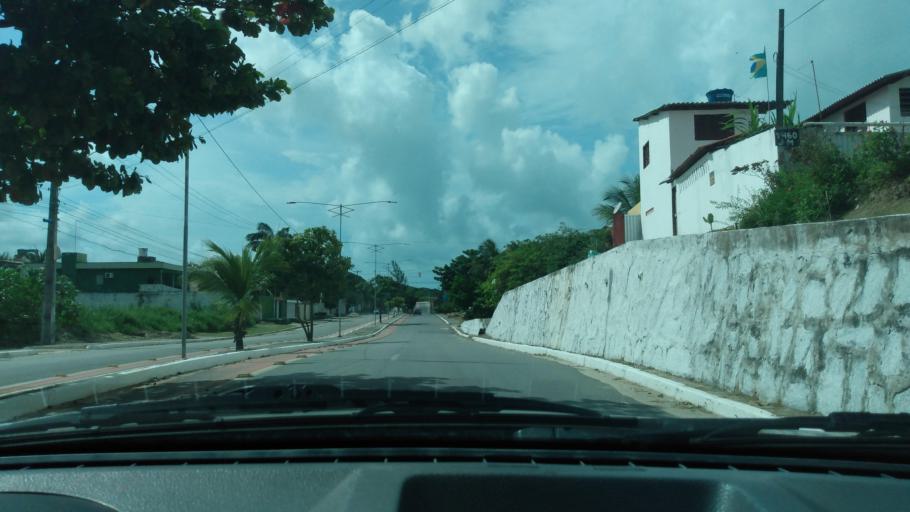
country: BR
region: Pernambuco
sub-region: Cabo De Santo Agostinho
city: Cabo
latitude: -8.3113
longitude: -34.9481
